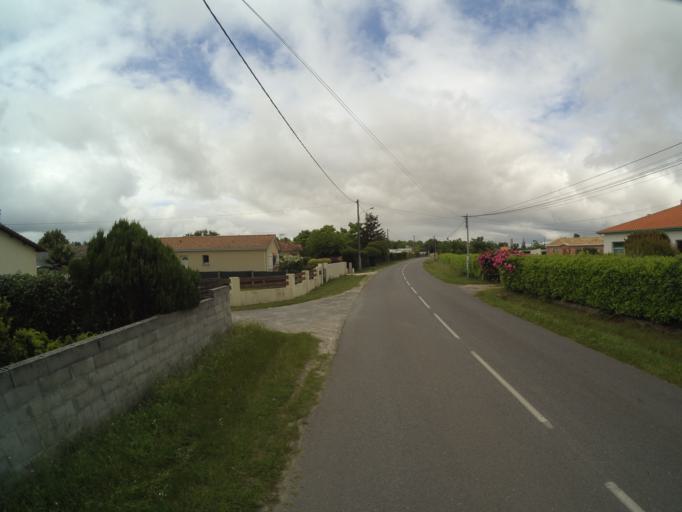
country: FR
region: Aquitaine
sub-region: Departement de la Gironde
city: Lamarque
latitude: 45.0924
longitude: -0.7235
